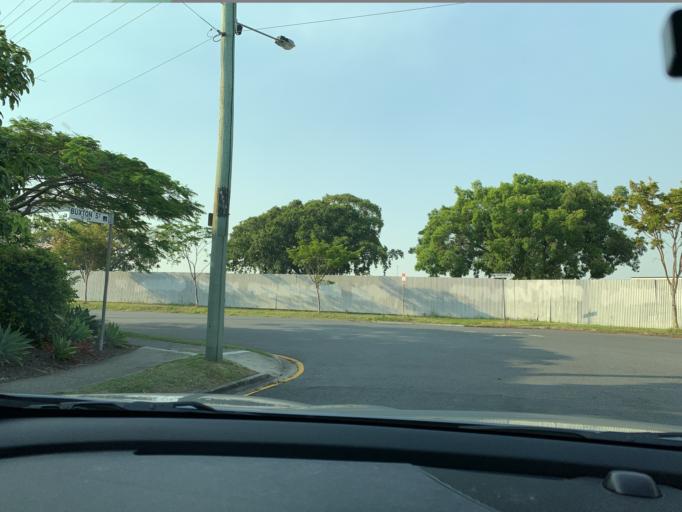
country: AU
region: Queensland
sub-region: Brisbane
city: Ascot
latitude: -27.4293
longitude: 153.0762
